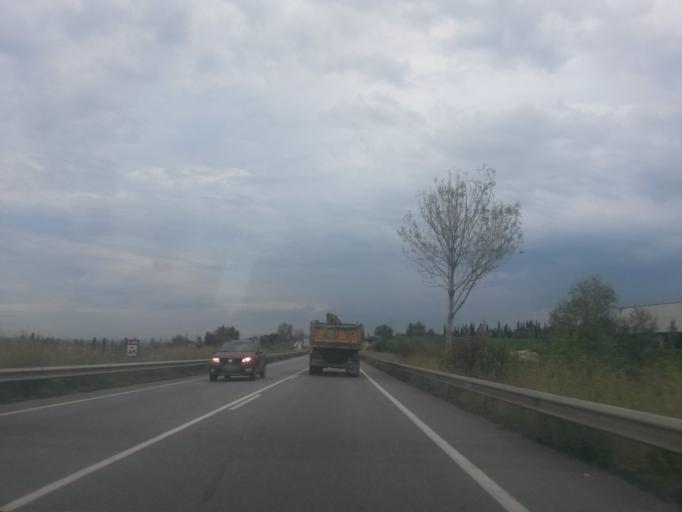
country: ES
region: Catalonia
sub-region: Provincia de Girona
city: Fontcoberta
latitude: 42.1195
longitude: 2.7868
